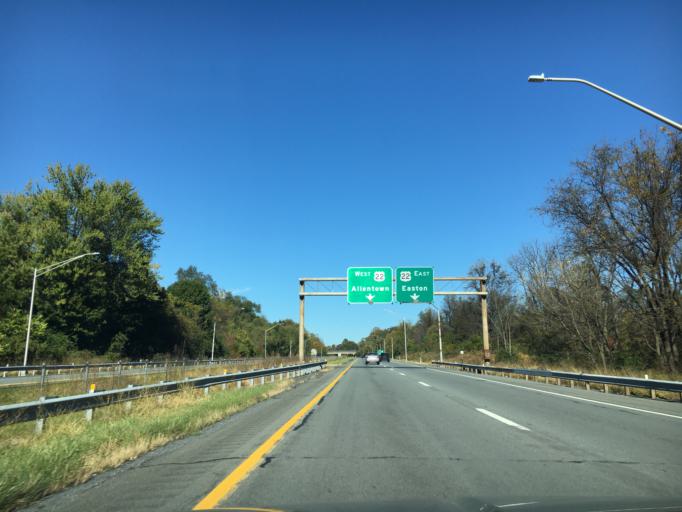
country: US
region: Pennsylvania
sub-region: Lehigh County
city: Fountain Hill
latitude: 40.6337
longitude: -75.4088
